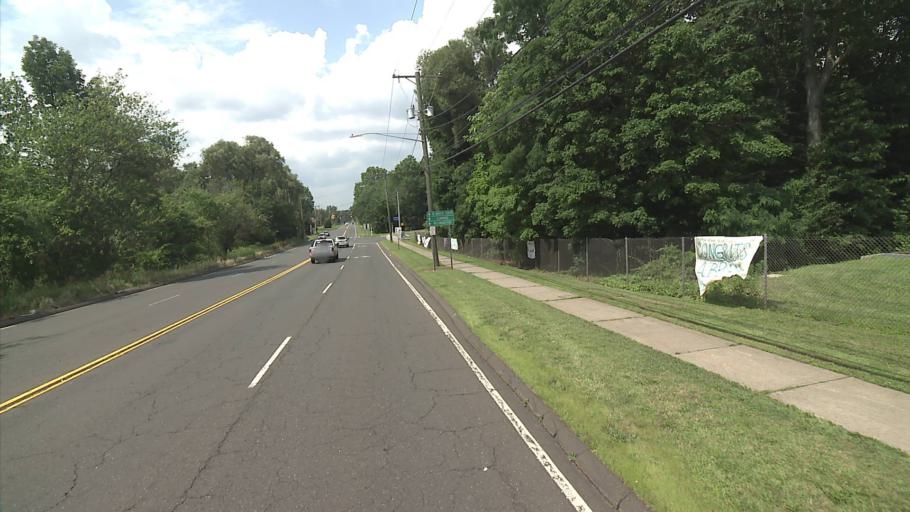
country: US
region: Connecticut
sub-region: Hartford County
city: Newington
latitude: 41.6770
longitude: -72.7294
